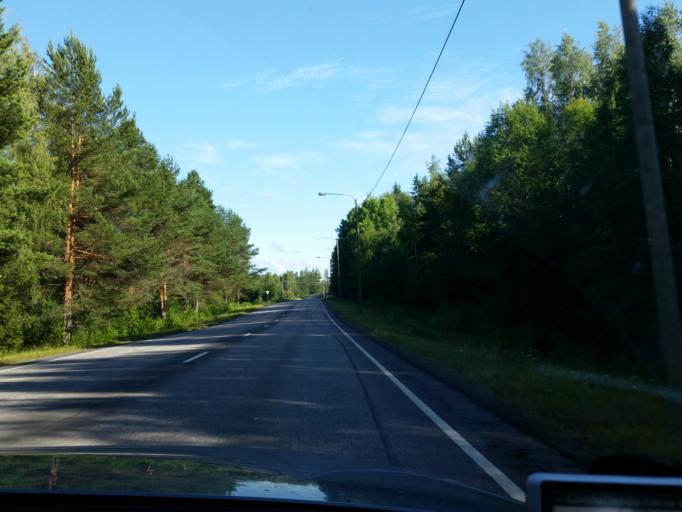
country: FI
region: Uusimaa
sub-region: Helsinki
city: Vihti
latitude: 60.3480
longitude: 24.1898
